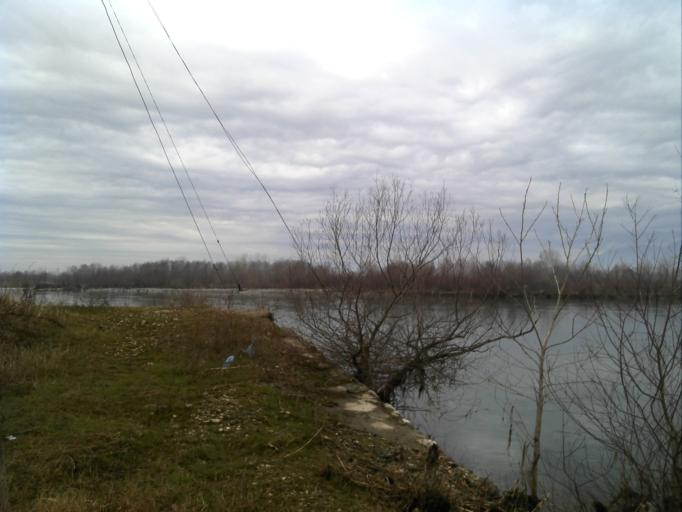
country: AL
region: Shkoder
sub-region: Rrethi i Shkodres
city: Dajc
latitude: 41.9906
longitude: 19.4400
